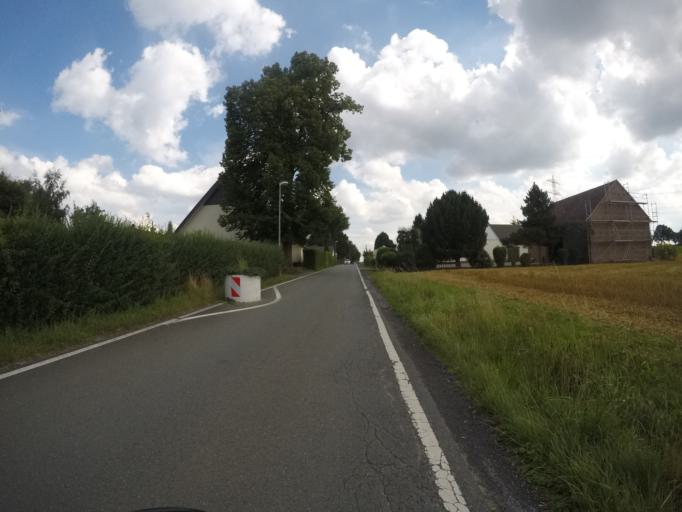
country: DE
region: North Rhine-Westphalia
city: Enger
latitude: 52.1042
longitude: 8.5870
